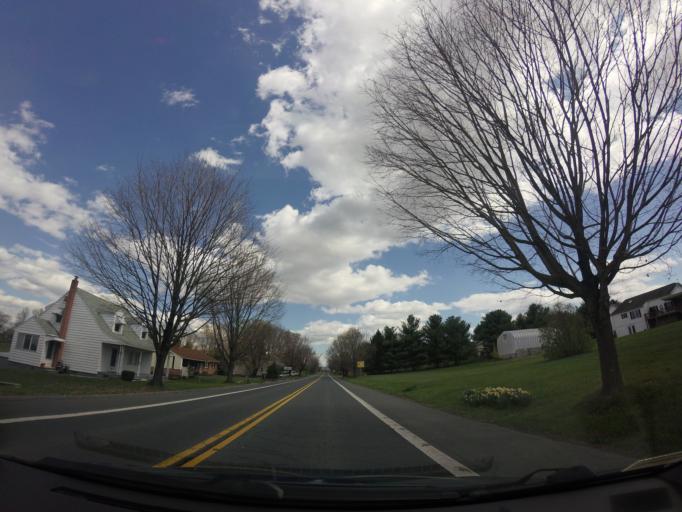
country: US
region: West Virginia
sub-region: Jefferson County
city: Shepherdstown
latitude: 39.4546
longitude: -77.7622
